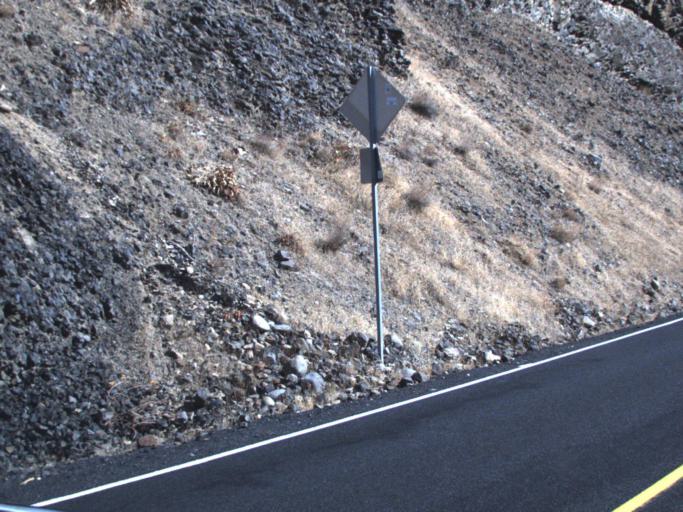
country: US
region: Washington
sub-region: Yakima County
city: Tieton
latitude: 46.7126
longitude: -120.8800
